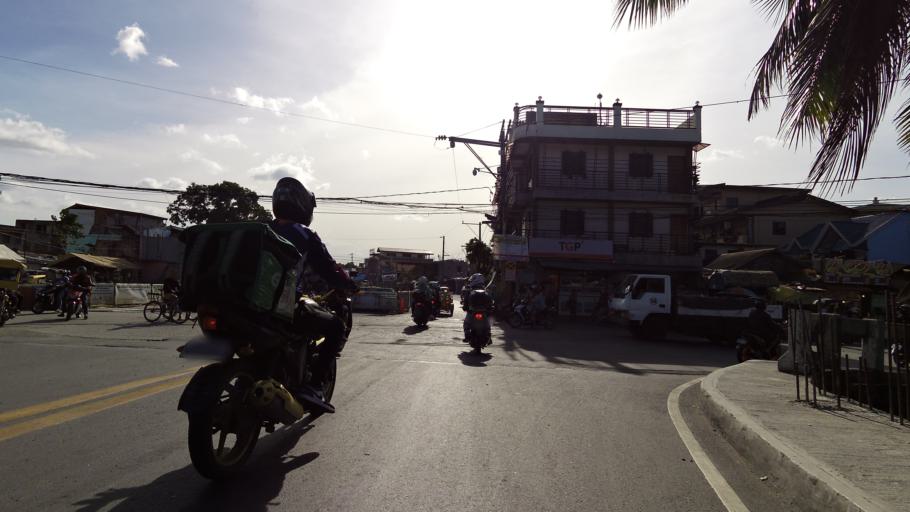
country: PH
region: Calabarzon
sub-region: Province of Rizal
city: Taytay
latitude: 14.5481
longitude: 121.1188
